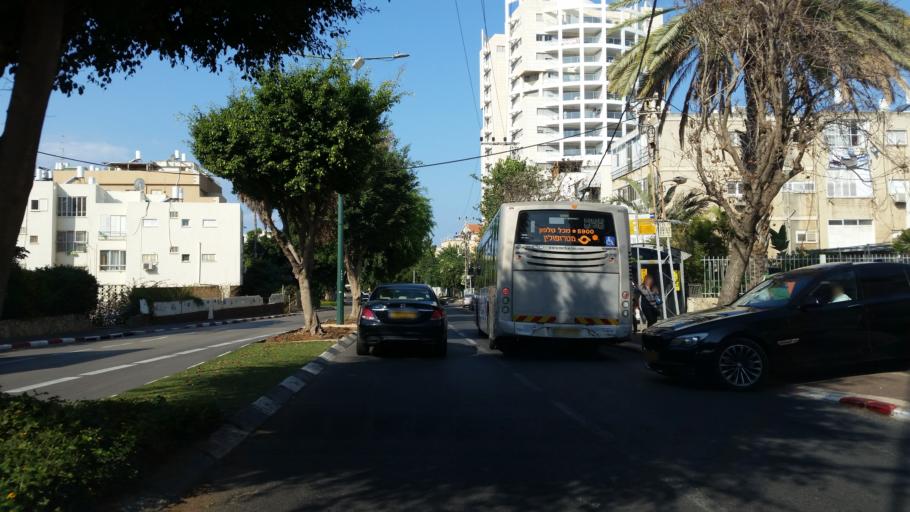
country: IL
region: Tel Aviv
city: Ramat HaSharon
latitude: 32.1611
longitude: 34.8419
